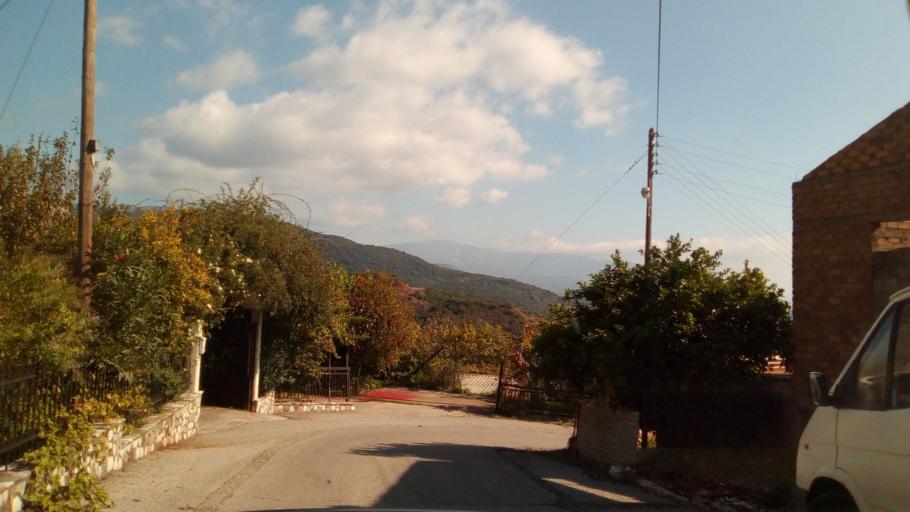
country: GR
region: West Greece
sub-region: Nomos Aitolias kai Akarnanias
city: Nafpaktos
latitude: 38.4210
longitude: 21.8671
